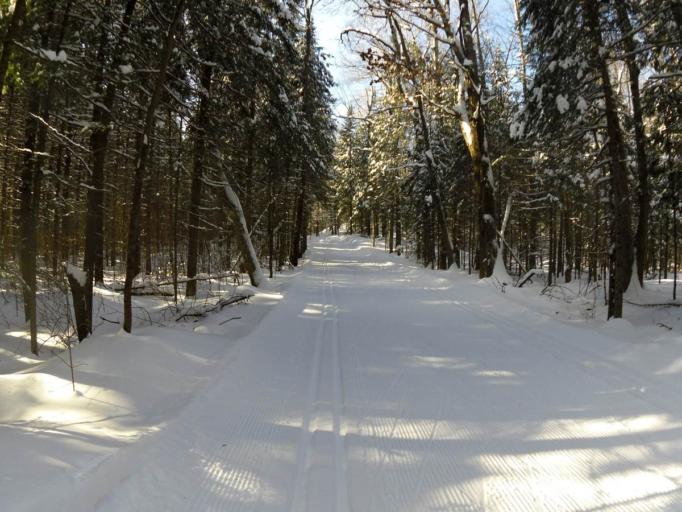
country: CA
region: Quebec
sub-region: Outaouais
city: Wakefield
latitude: 45.6282
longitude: -75.9771
